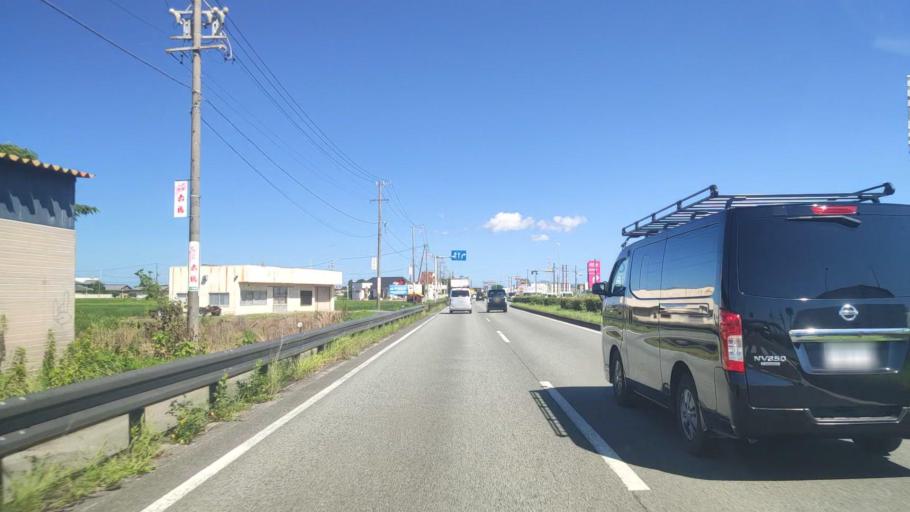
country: JP
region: Mie
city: Hisai-motomachi
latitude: 34.5980
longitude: 136.5366
